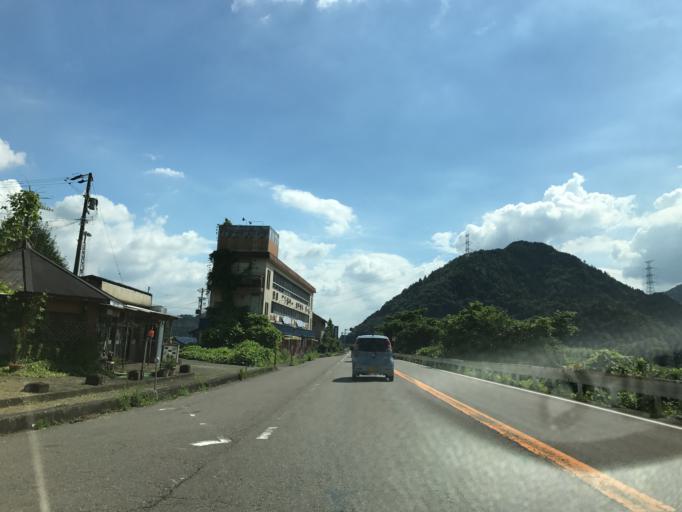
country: JP
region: Gifu
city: Mino
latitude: 35.5664
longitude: 136.9175
